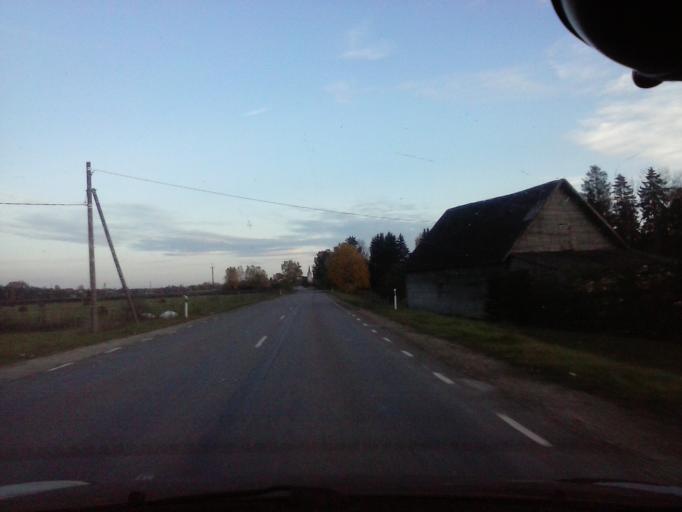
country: EE
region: Raplamaa
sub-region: Maerjamaa vald
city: Marjamaa
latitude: 58.9211
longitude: 24.4103
